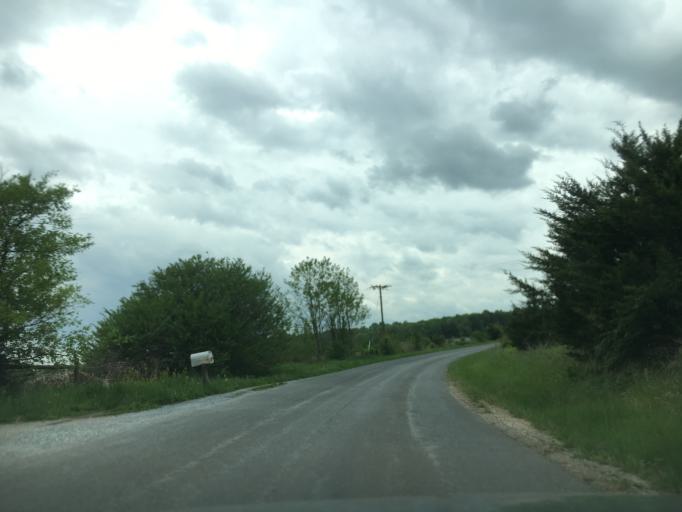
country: US
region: Virginia
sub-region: Campbell County
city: Rustburg
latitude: 37.1741
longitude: -79.0445
